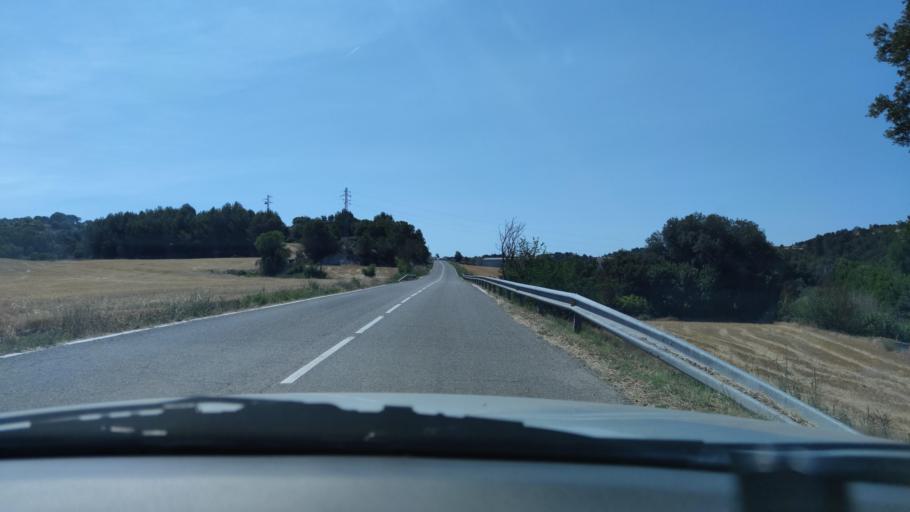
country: ES
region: Catalonia
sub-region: Provincia de Lleida
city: Sant Guim de Freixenet
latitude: 41.6268
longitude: 1.3454
